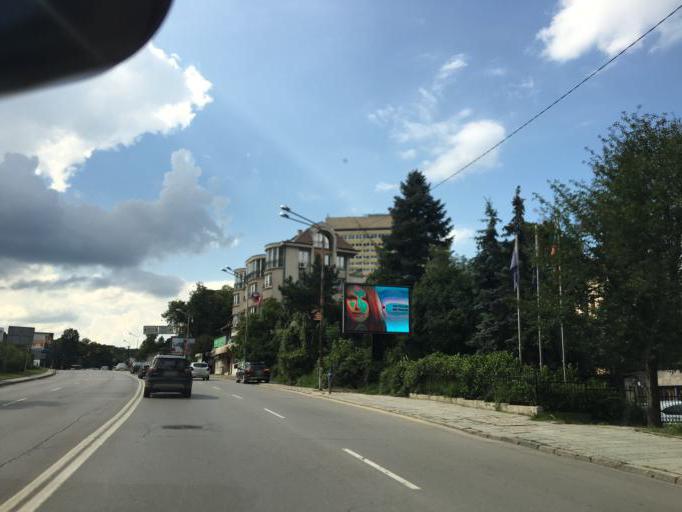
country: BG
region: Sofia-Capital
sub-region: Stolichna Obshtina
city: Sofia
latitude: 42.6718
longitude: 23.3506
